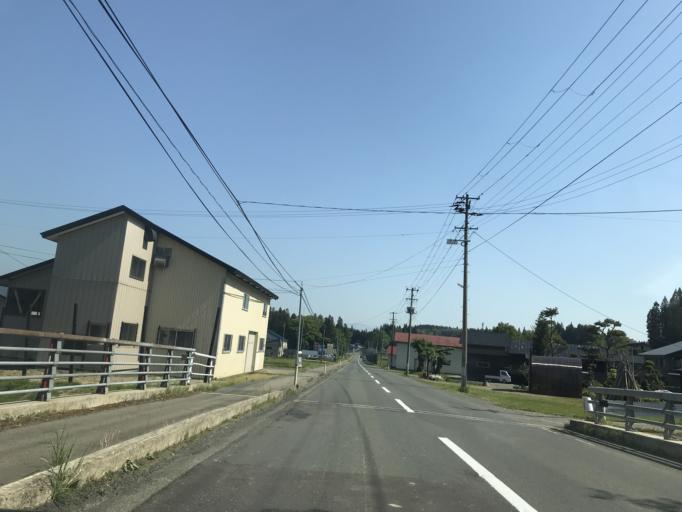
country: JP
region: Akita
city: Yokotemachi
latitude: 39.4152
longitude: 140.7480
